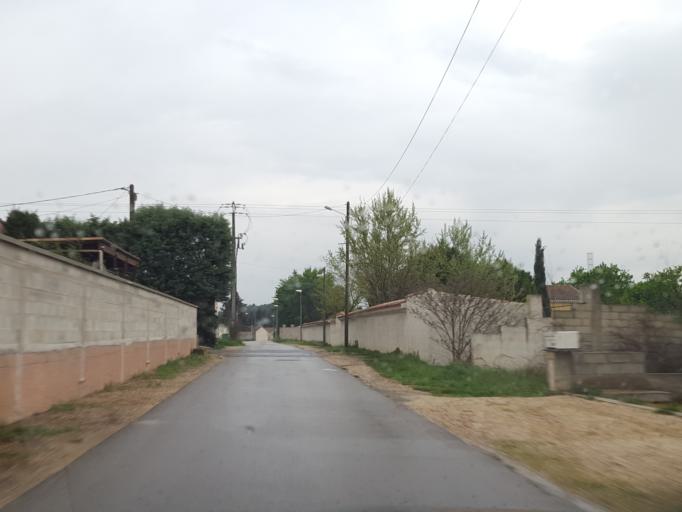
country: FR
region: Provence-Alpes-Cote d'Azur
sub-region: Departement du Vaucluse
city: Saint-Saturnin-les-Avignon
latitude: 43.9654
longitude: 4.9281
